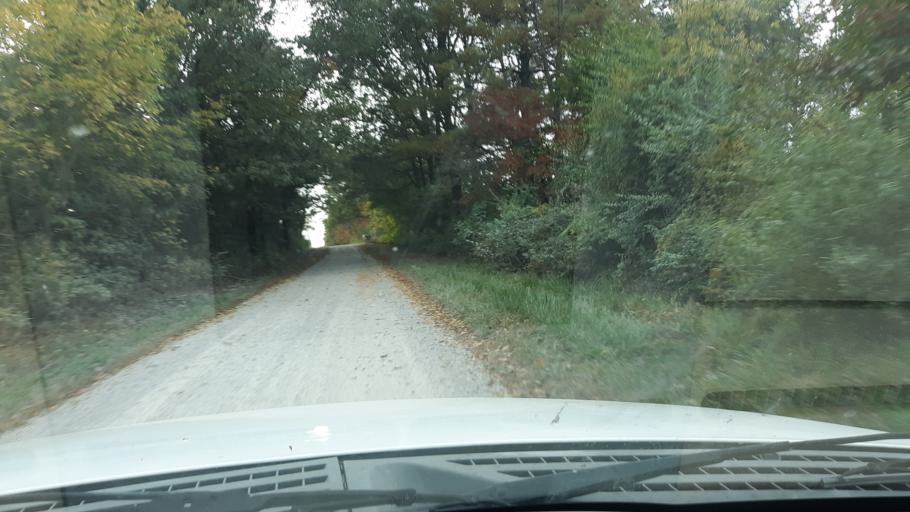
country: US
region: Illinois
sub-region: Saline County
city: Eldorado
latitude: 37.8343
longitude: -88.5007
